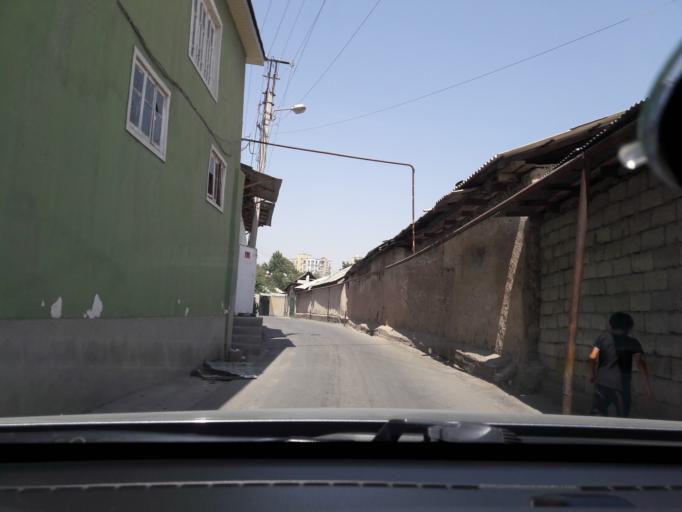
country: TJ
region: Dushanbe
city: Dushanbe
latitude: 38.5860
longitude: 68.7373
